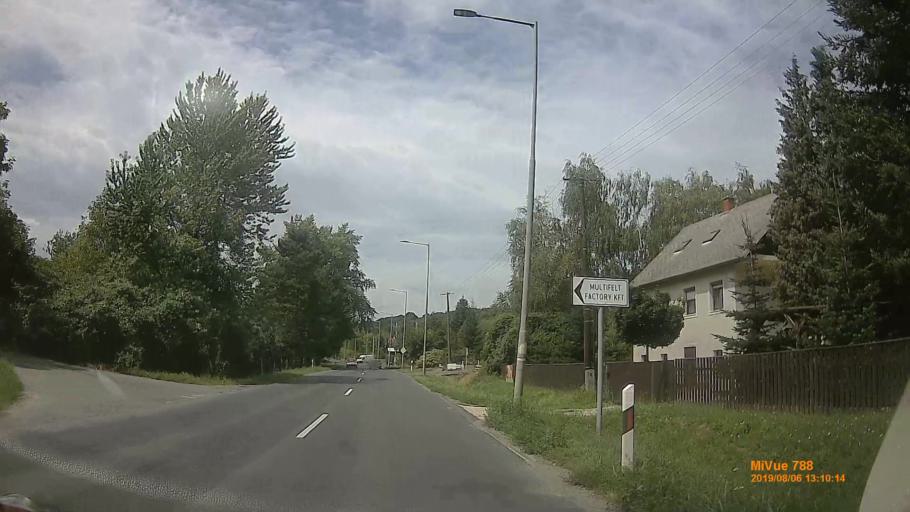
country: HU
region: Vas
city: Koszeg
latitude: 47.4040
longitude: 16.5347
